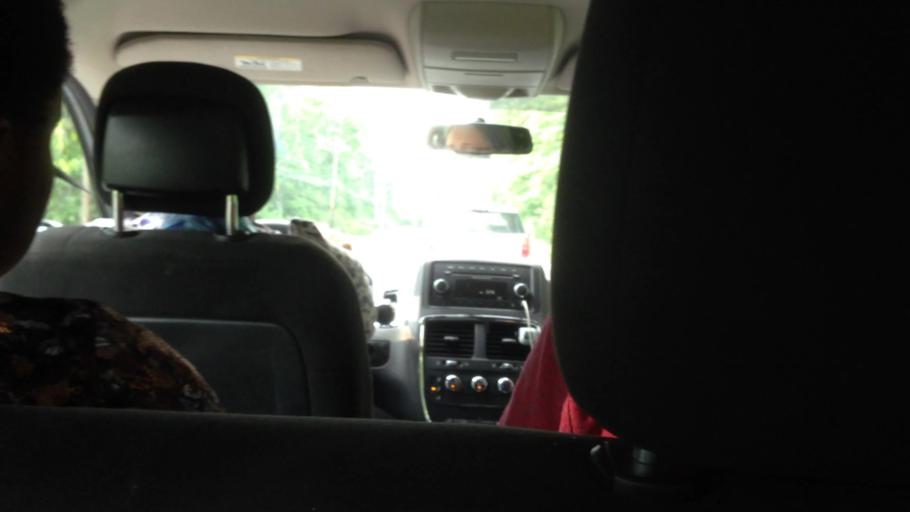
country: US
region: New York
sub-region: Dutchess County
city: Red Hook
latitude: 41.9922
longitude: -73.9103
